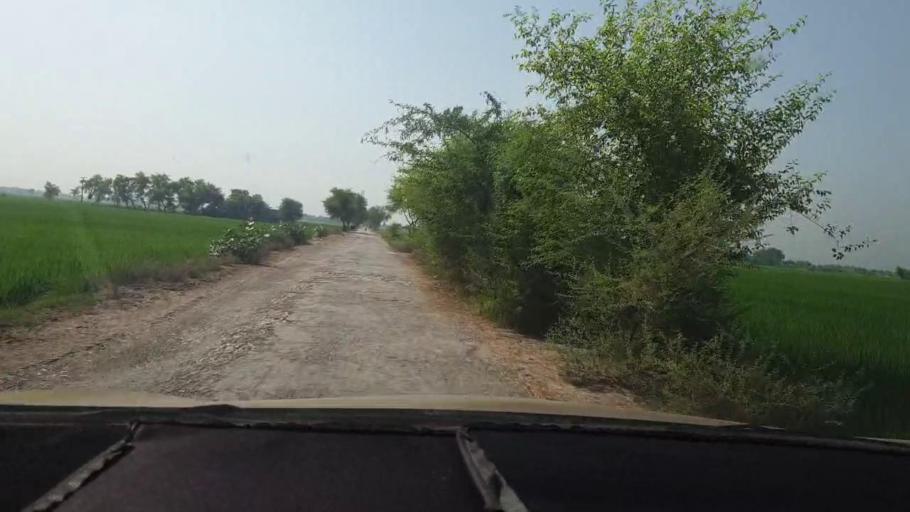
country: PK
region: Sindh
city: Kambar
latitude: 27.5672
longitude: 68.0567
